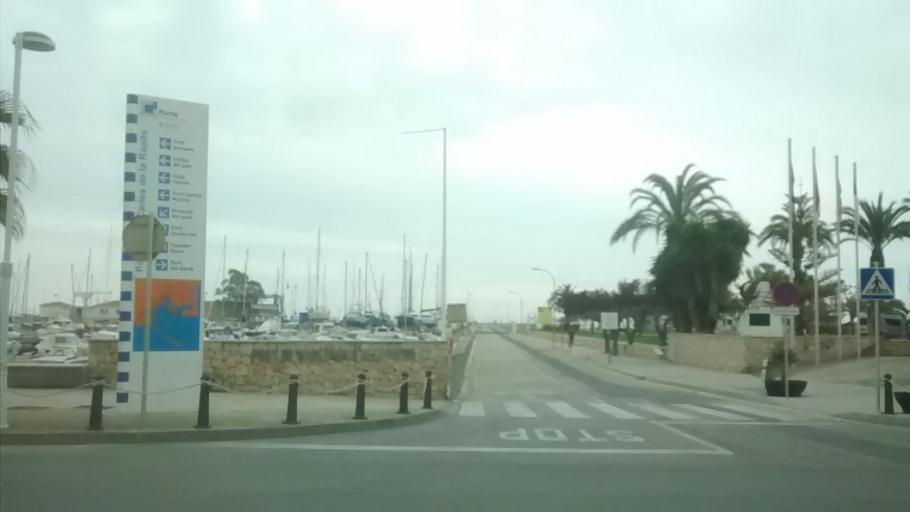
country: ES
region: Catalonia
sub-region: Provincia de Tarragona
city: Sant Carles de la Rapita
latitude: 40.6164
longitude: 0.5930
